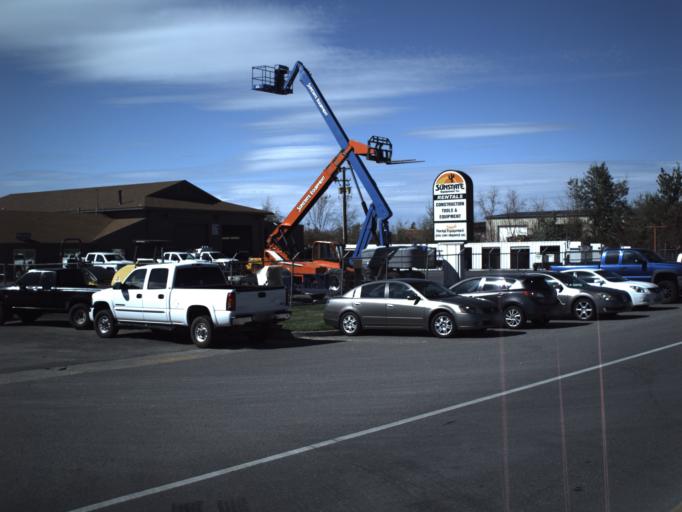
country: US
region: Utah
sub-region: Davis County
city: North Salt Lake
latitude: 40.8113
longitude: -111.9387
